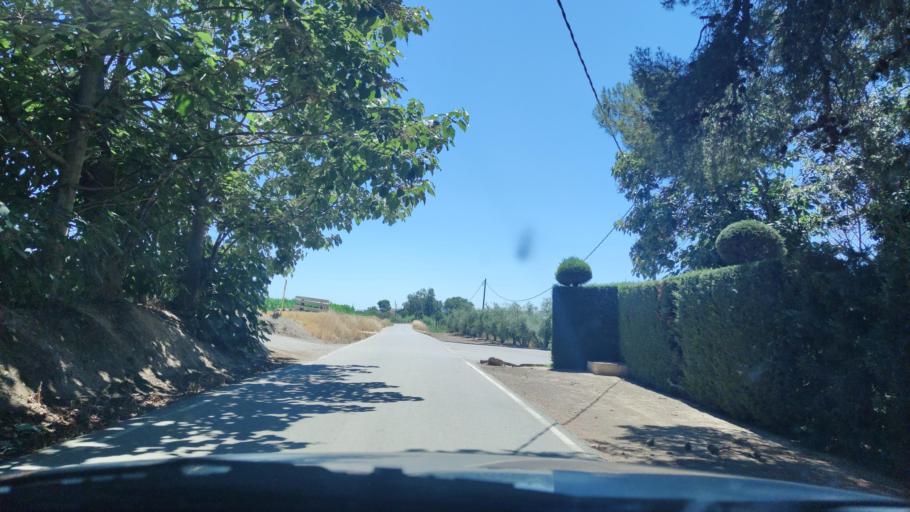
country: ES
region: Catalonia
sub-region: Provincia de Lleida
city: Alcoletge
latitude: 41.6469
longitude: 0.6648
